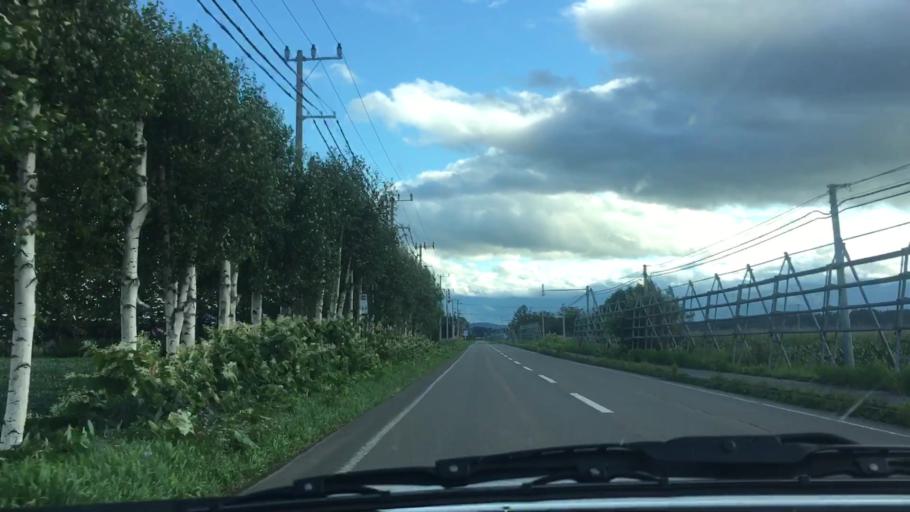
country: JP
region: Hokkaido
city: Otofuke
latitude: 43.1417
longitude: 142.8962
